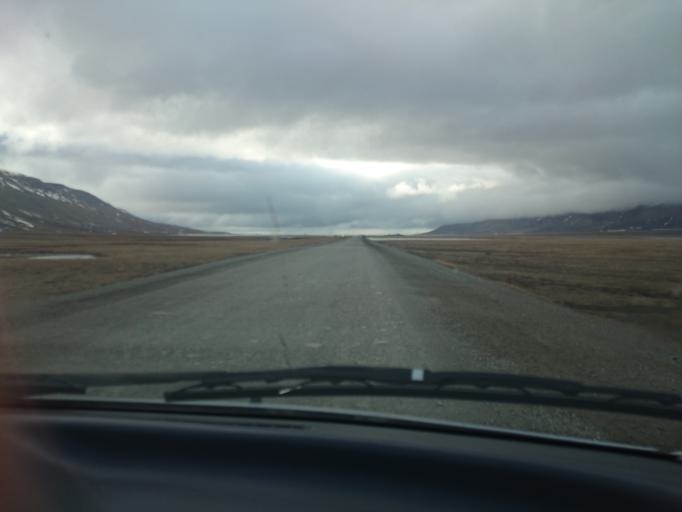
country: SJ
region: Svalbard
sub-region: Spitsbergen
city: Longyearbyen
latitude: 78.1922
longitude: 15.8638
